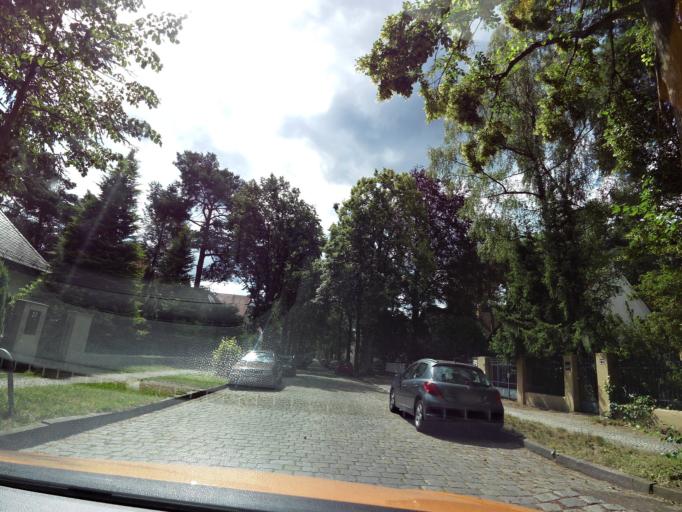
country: DE
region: Berlin
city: Nikolassee
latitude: 52.4339
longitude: 13.2222
